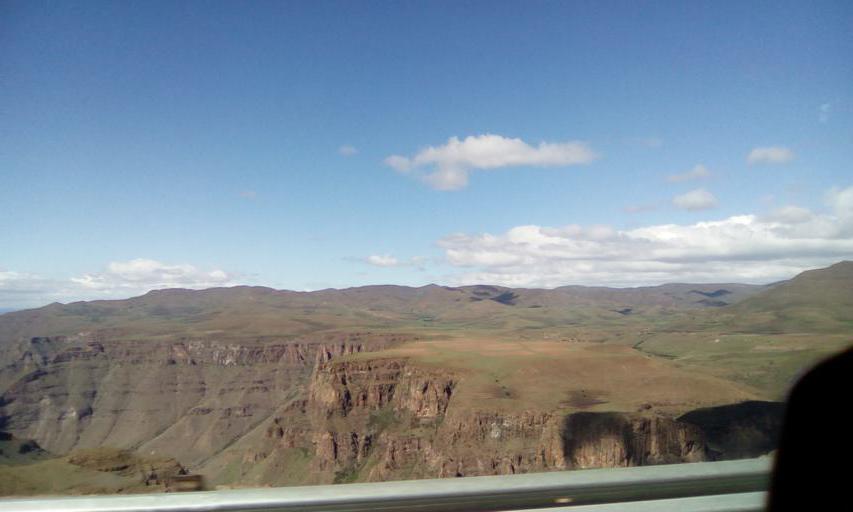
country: LS
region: Maseru
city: Nako
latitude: -29.8771
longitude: 28.0760
